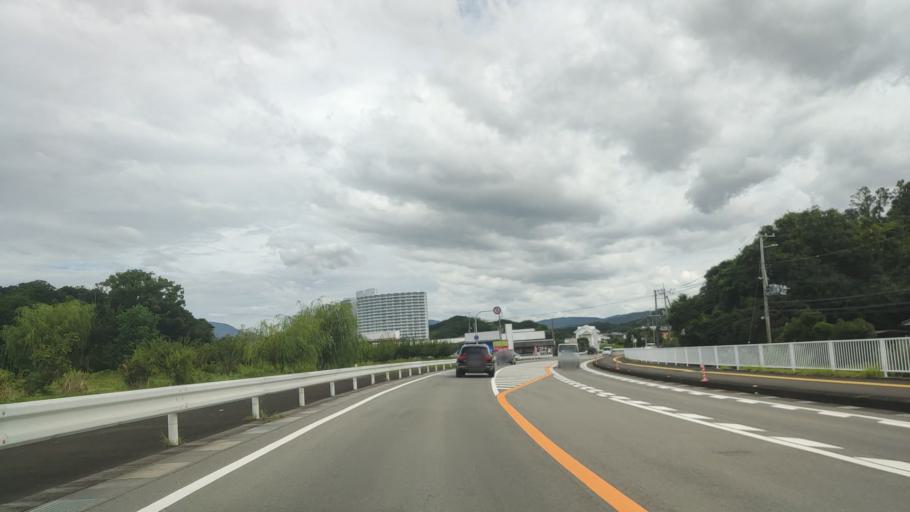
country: JP
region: Wakayama
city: Tanabe
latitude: 33.7008
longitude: 135.3894
